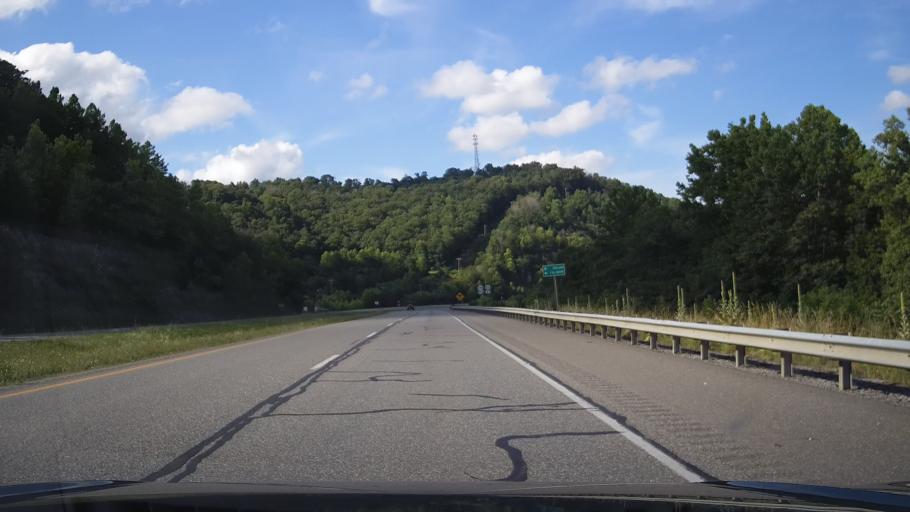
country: US
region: Kentucky
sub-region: Lawrence County
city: Louisa
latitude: 38.1667
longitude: -82.6451
